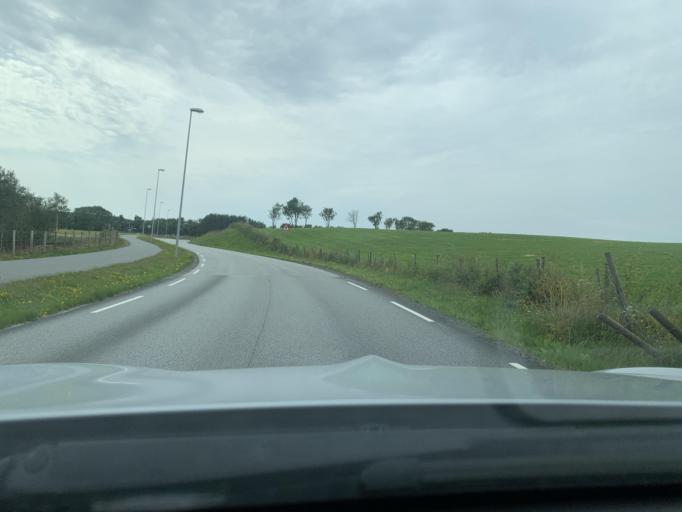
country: NO
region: Rogaland
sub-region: Time
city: Bryne
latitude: 58.7628
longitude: 5.7116
